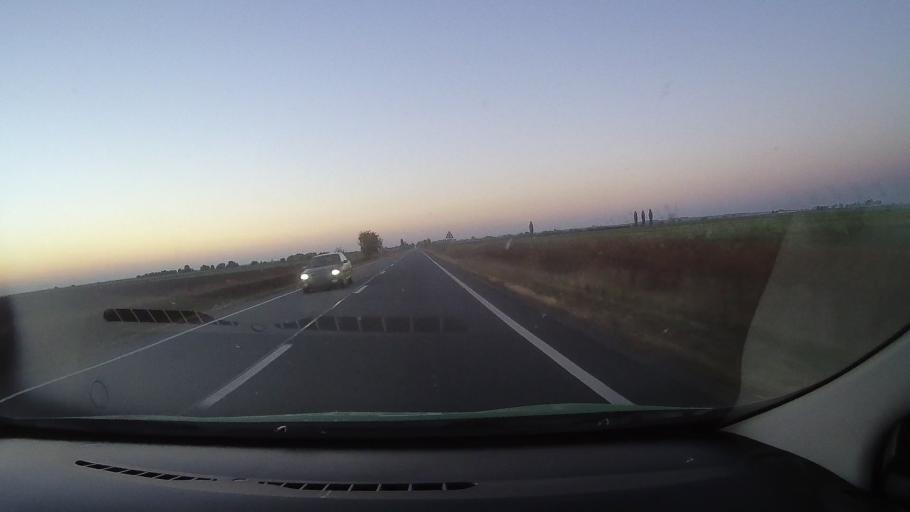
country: RO
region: Bihor
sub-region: Comuna Valea lui Mihai
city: Valea lui Mihai
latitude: 47.4841
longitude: 22.1602
